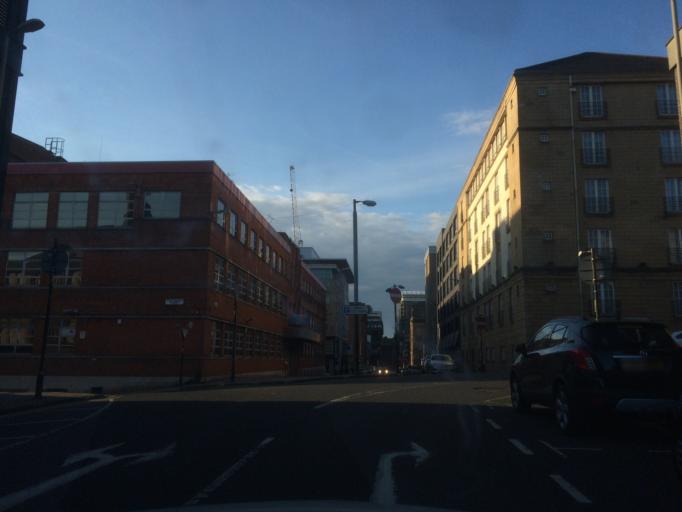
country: GB
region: Scotland
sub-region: Glasgow City
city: Glasgow
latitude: 55.8631
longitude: -4.2656
